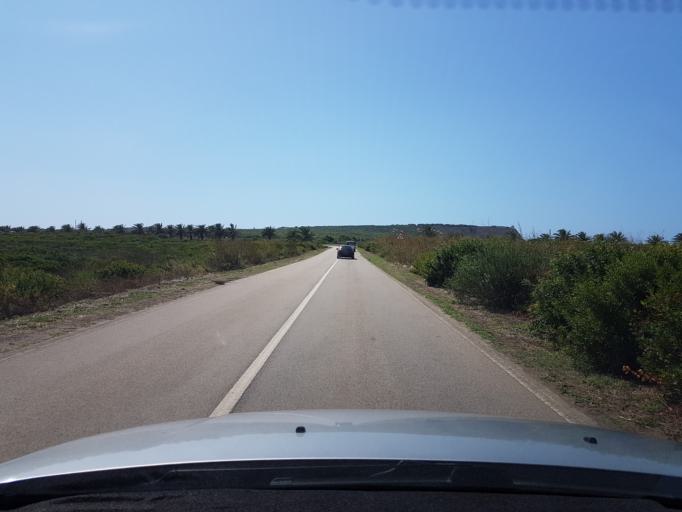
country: IT
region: Sardinia
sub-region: Provincia di Oristano
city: Riola Sardo
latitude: 40.0408
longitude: 8.4040
